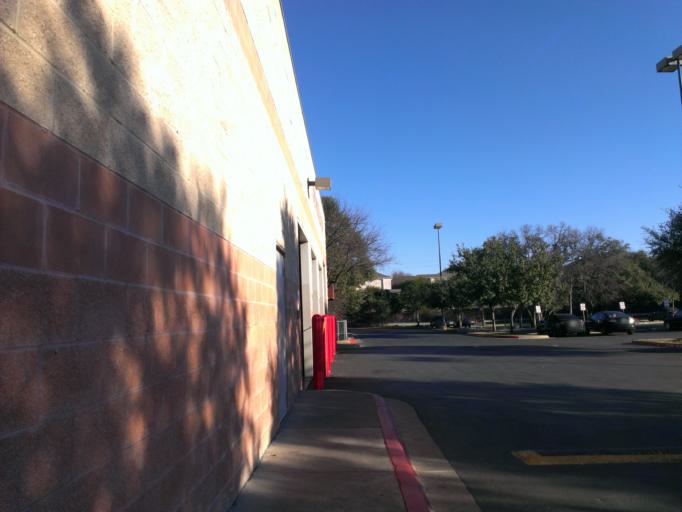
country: US
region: Texas
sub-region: Williamson County
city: Jollyville
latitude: 30.3963
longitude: -97.7441
